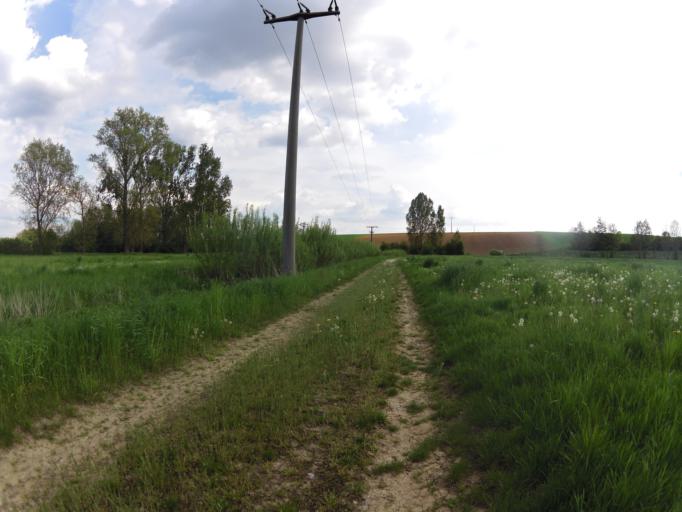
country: DE
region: Bavaria
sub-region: Regierungsbezirk Unterfranken
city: Giebelstadt
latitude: 49.6250
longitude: 9.9439
